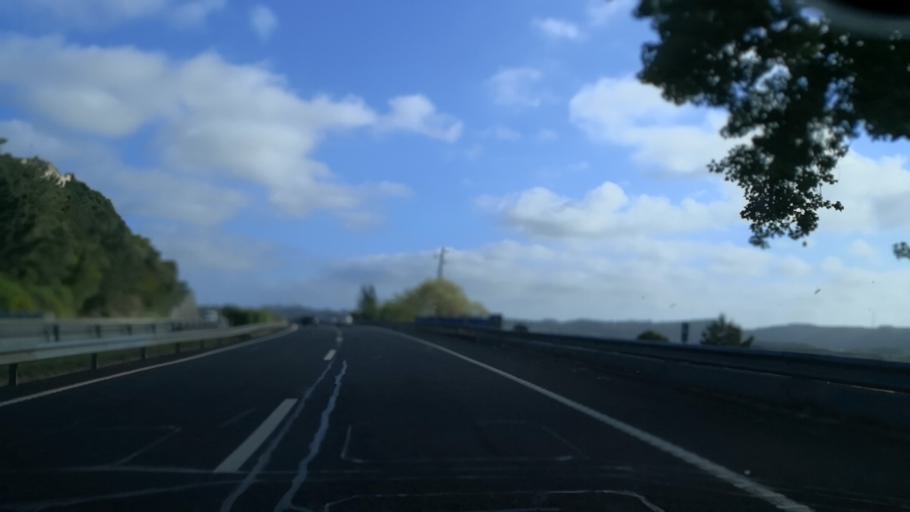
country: PT
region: Leiria
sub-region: Obidos
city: Obidos
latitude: 39.3245
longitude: -9.1763
